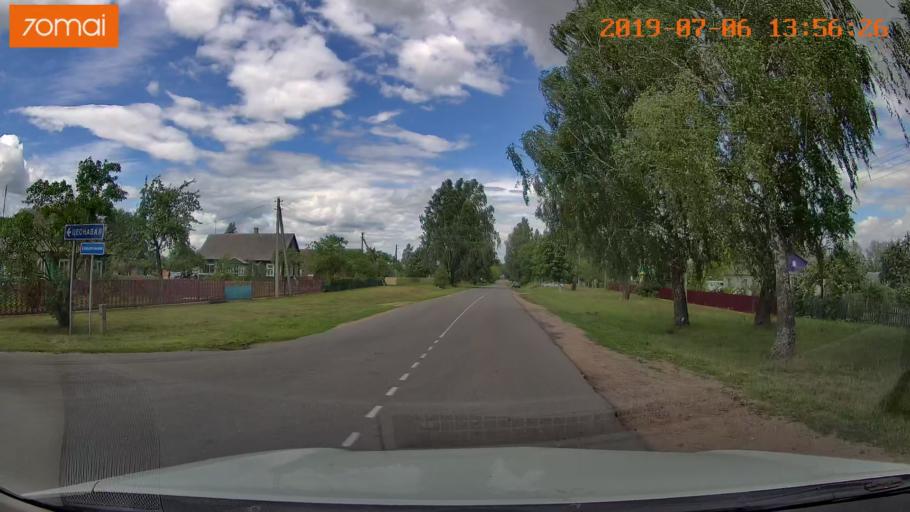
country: BY
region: Minsk
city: Ivyanyets
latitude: 53.7653
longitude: 26.8041
